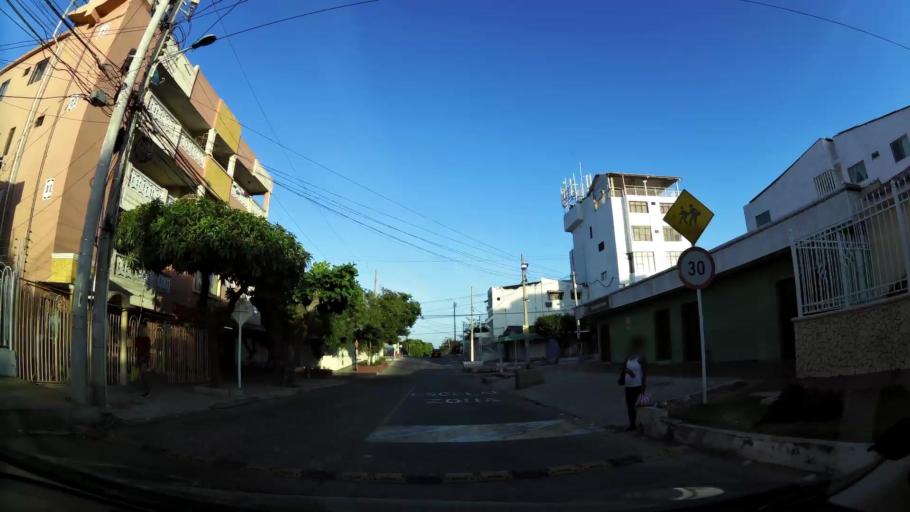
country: CO
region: Atlantico
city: Barranquilla
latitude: 10.9728
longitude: -74.8020
